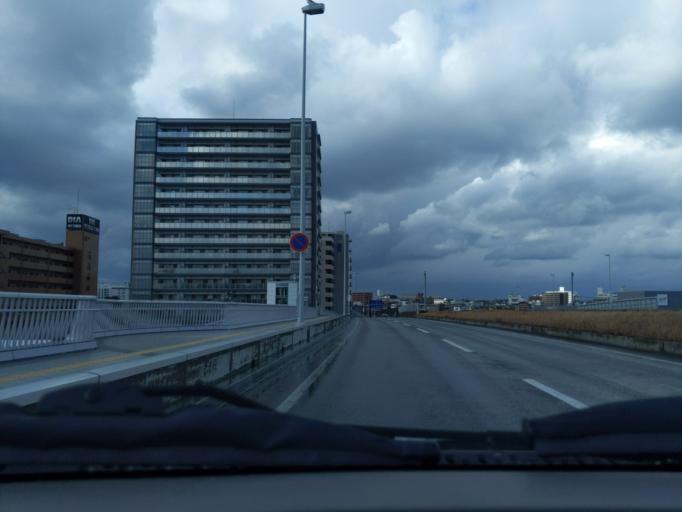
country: JP
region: Niigata
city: Niigata-shi
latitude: 37.9232
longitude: 139.0555
